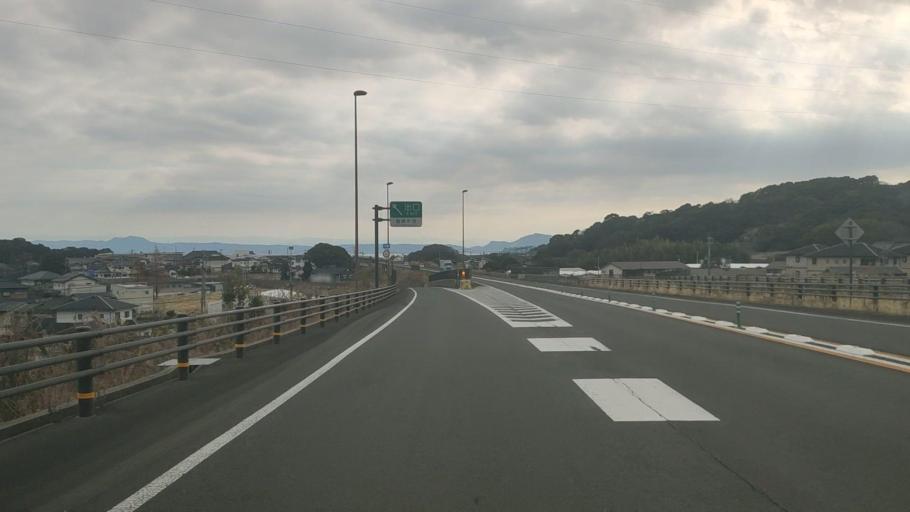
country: JP
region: Nagasaki
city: Shimabara
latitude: 32.7635
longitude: 130.3619
